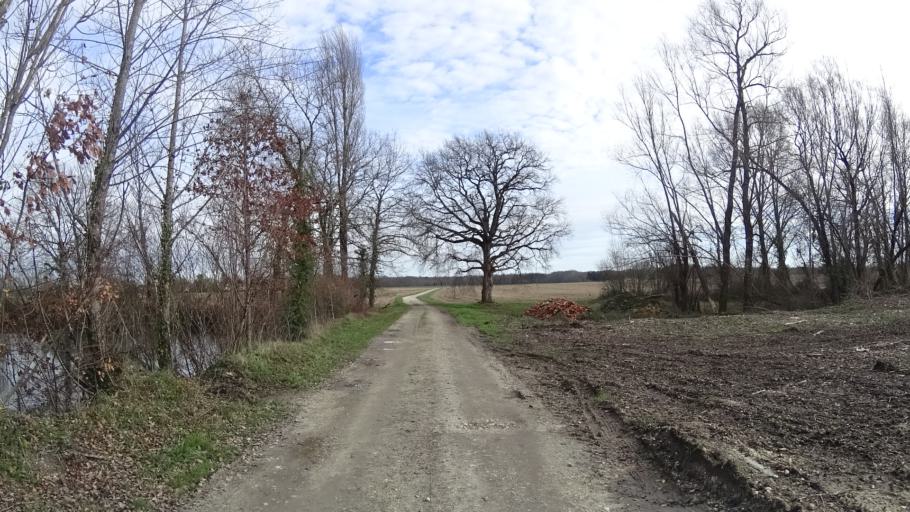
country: FR
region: Aquitaine
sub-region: Departement de la Dordogne
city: Saint-Aulaye
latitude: 45.2234
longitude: 0.1410
